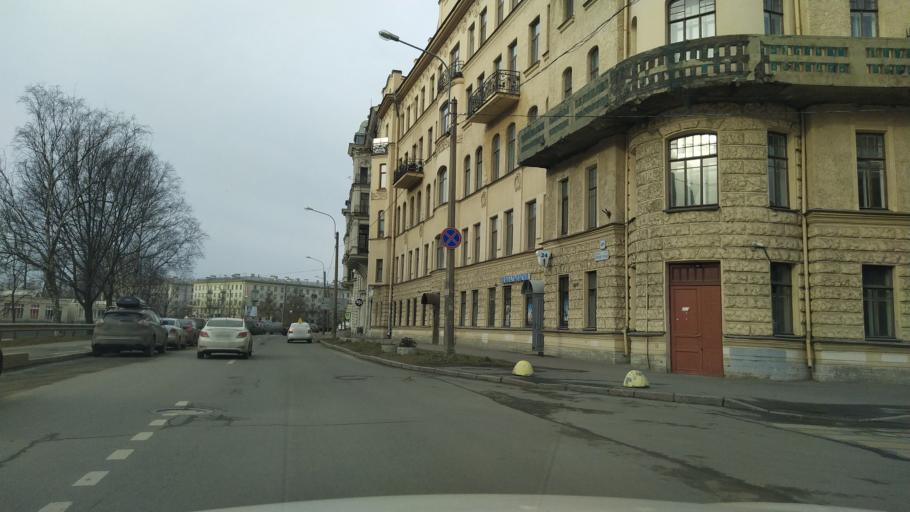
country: RU
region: Leningrad
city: Chernaya Rechka
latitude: 59.9855
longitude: 30.3056
